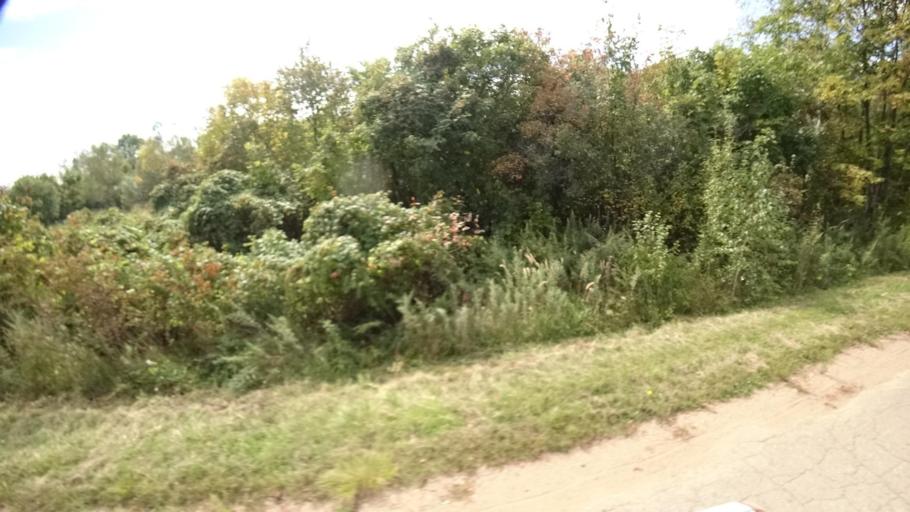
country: RU
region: Primorskiy
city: Yakovlevka
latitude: 44.7100
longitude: 133.6343
